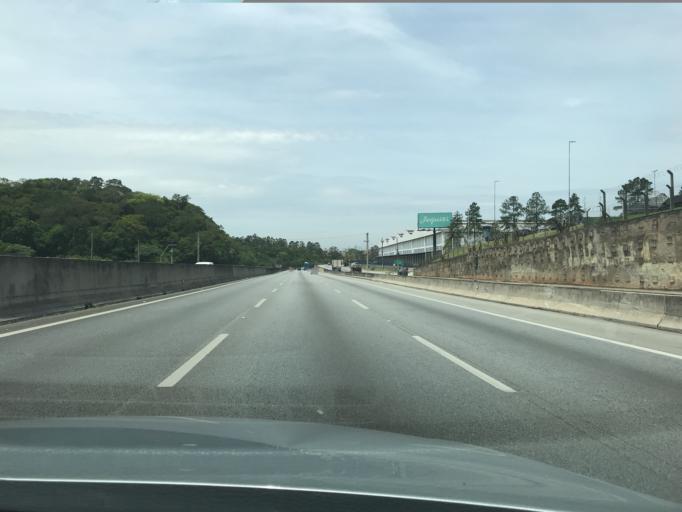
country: BR
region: Sao Paulo
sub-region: Osasco
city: Osasco
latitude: -23.4728
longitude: -46.7753
